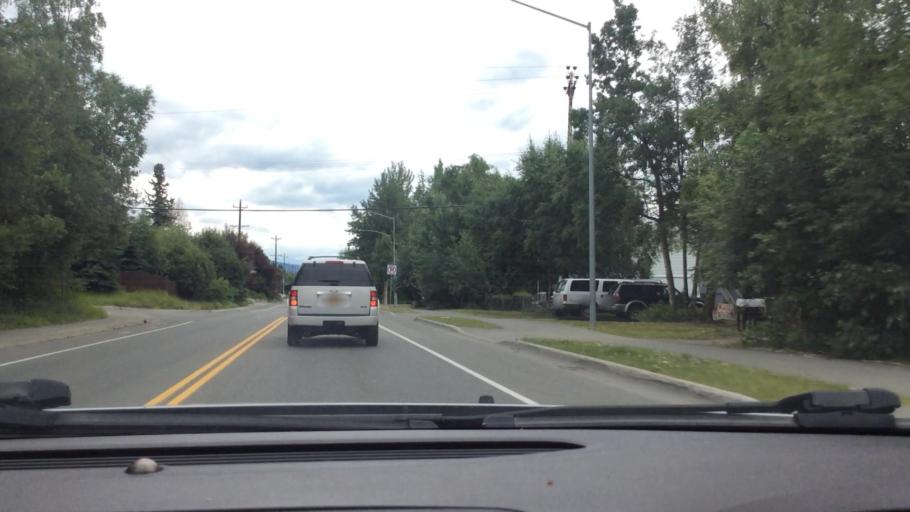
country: US
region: Alaska
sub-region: Anchorage Municipality
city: Elmendorf Air Force Base
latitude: 61.2174
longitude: -149.7560
